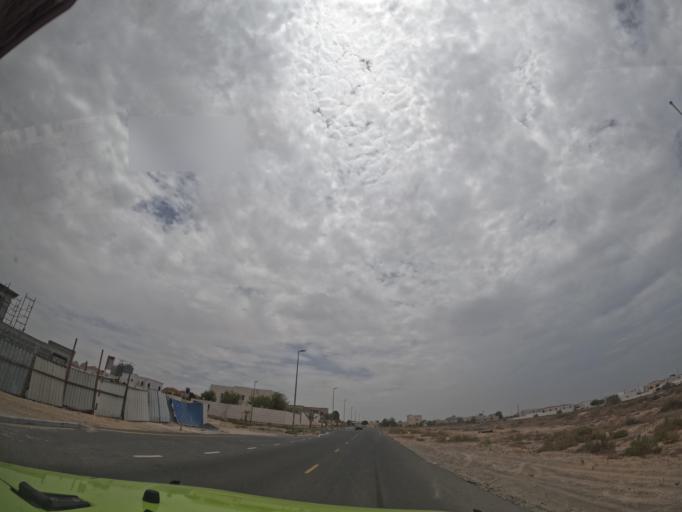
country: AE
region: Dubai
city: Dubai
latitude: 25.1288
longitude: 55.3694
